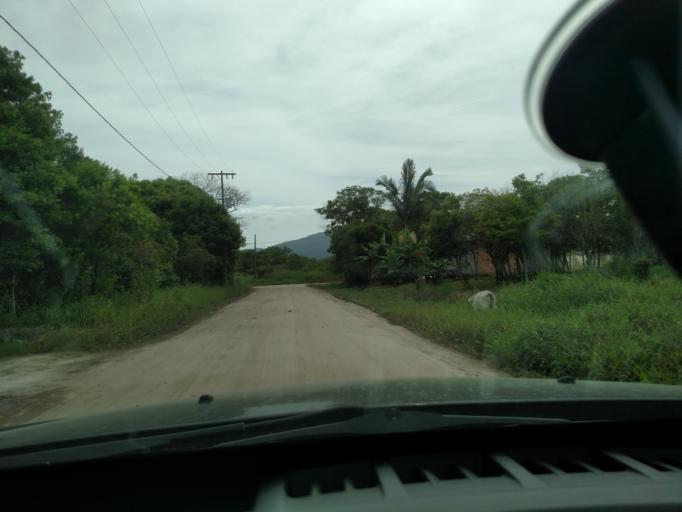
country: BR
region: Santa Catarina
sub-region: Porto Belo
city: Porto Belo
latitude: -27.1840
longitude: -48.5068
